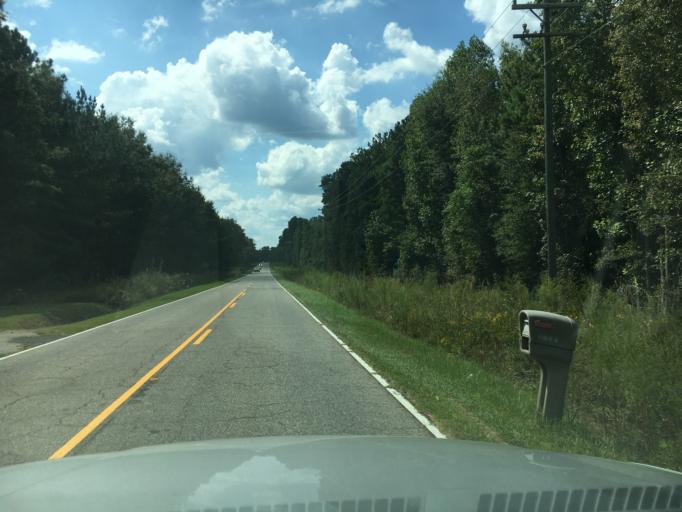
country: US
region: South Carolina
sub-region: Greenwood County
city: Greenwood
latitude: 34.0818
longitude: -82.1356
